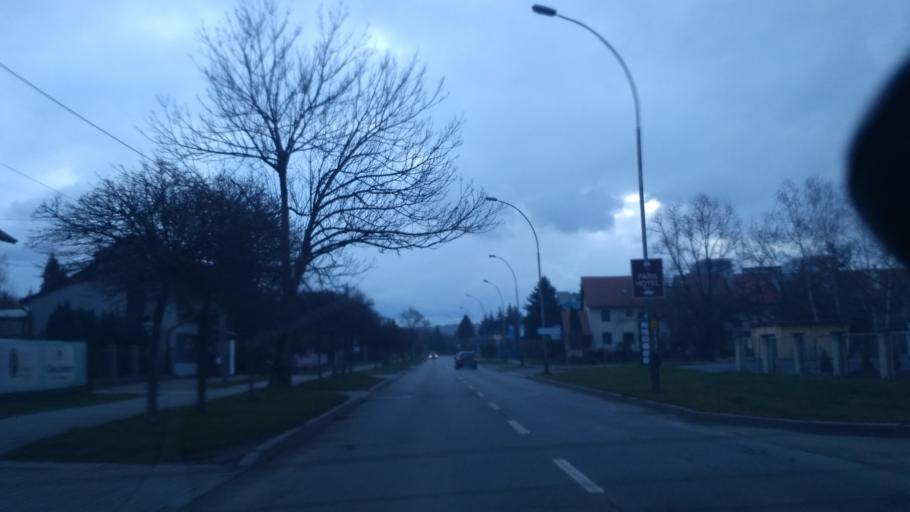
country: PL
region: Subcarpathian Voivodeship
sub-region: Rzeszow
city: Rzeszow
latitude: 50.0337
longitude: 22.0413
